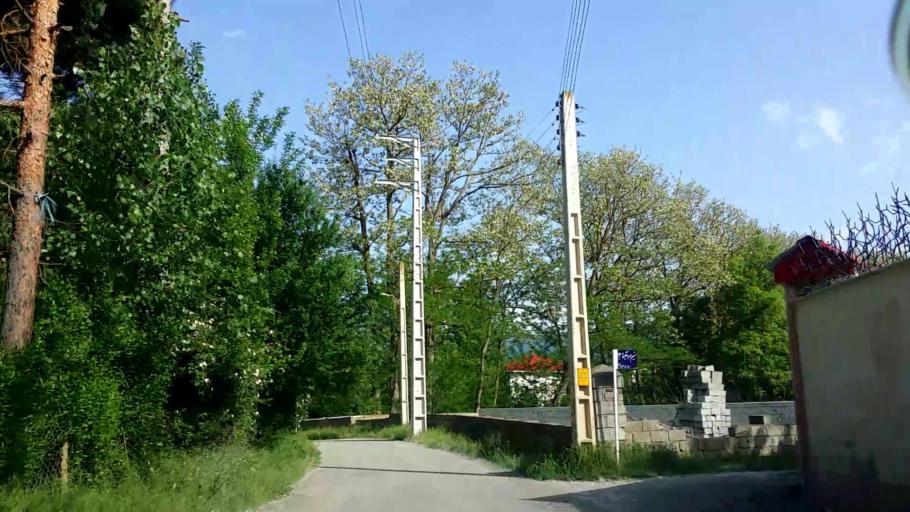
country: IR
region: Mazandaran
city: `Abbasabad
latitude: 36.5230
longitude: 51.1747
